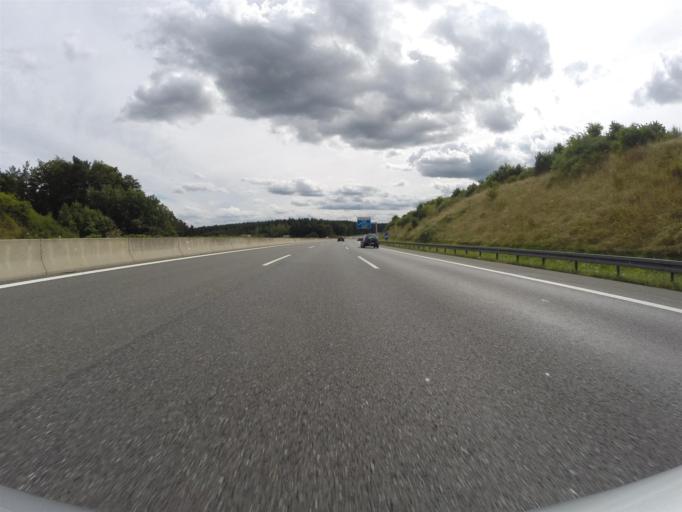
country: DE
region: Bavaria
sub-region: Upper Franconia
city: Pegnitz
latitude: 49.7353
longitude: 11.5149
